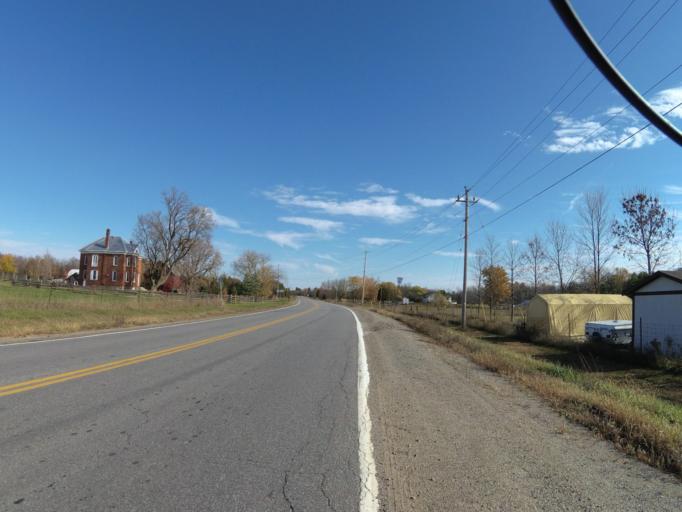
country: CA
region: Ontario
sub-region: Lanark County
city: Smiths Falls
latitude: 44.8355
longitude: -75.9383
